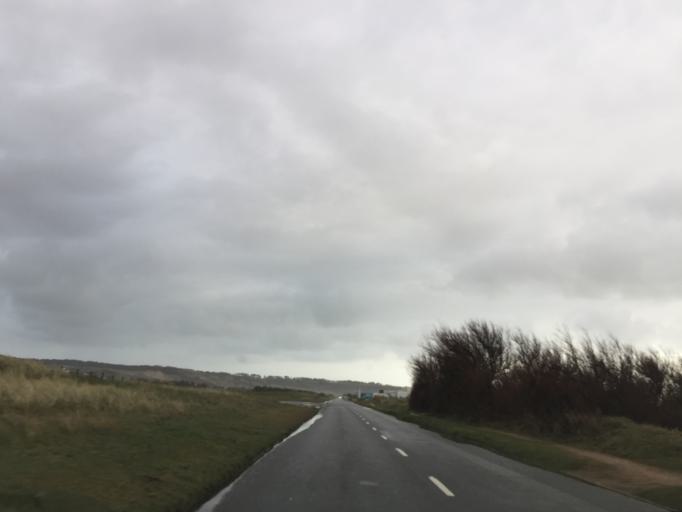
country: JE
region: St Helier
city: Saint Helier
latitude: 49.2127
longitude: -2.2242
